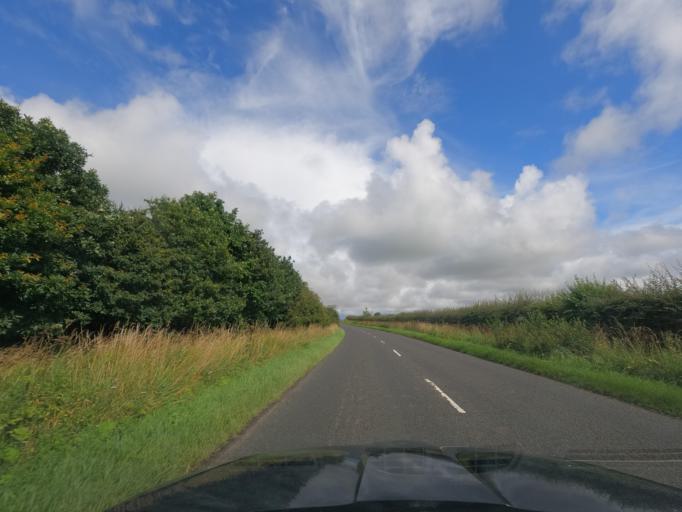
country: GB
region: England
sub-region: Northumberland
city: Lowick
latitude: 55.6086
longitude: -2.0001
